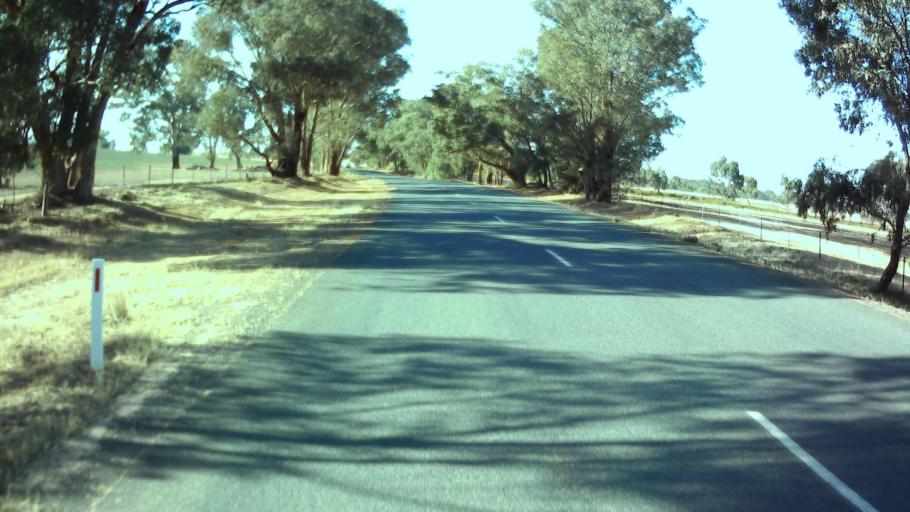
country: AU
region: New South Wales
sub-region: Weddin
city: Grenfell
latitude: -33.9808
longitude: 148.1404
